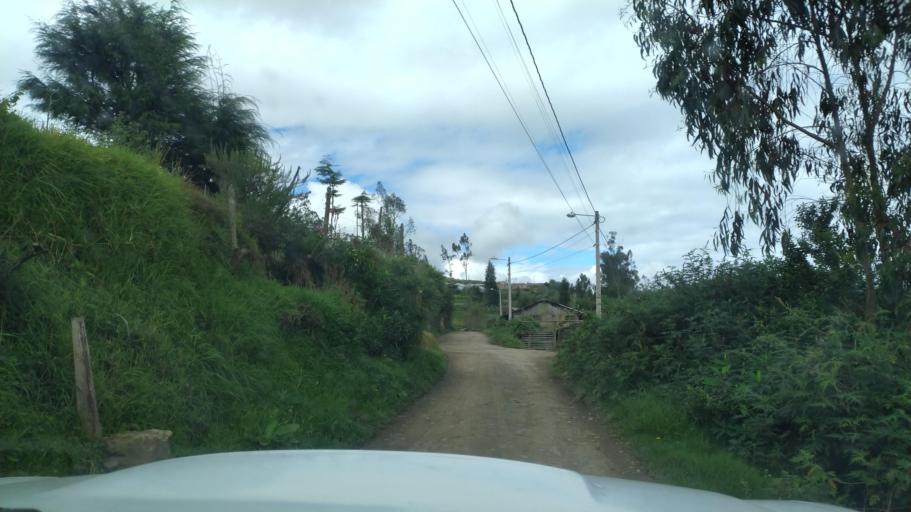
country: EC
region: Chimborazo
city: Riobamba
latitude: -1.6611
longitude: -78.5707
